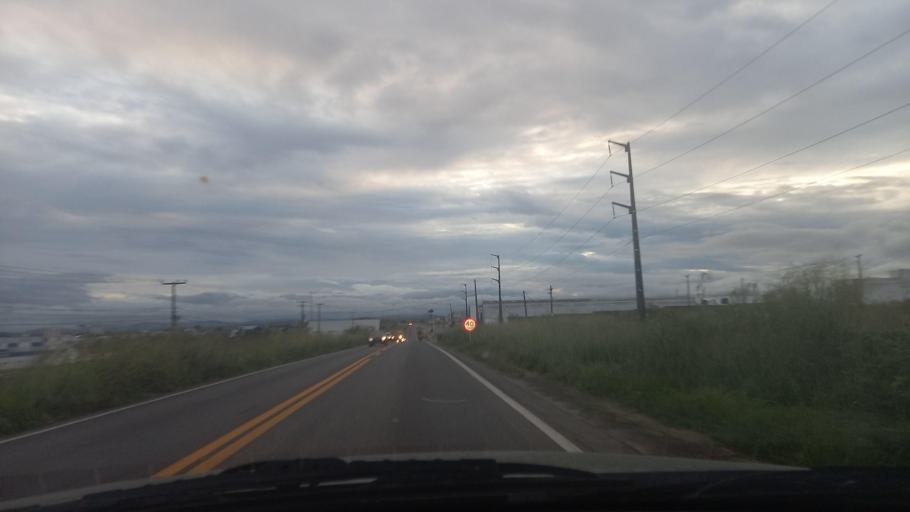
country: BR
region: Pernambuco
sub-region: Caruaru
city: Caruaru
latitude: -8.2547
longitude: -35.9664
